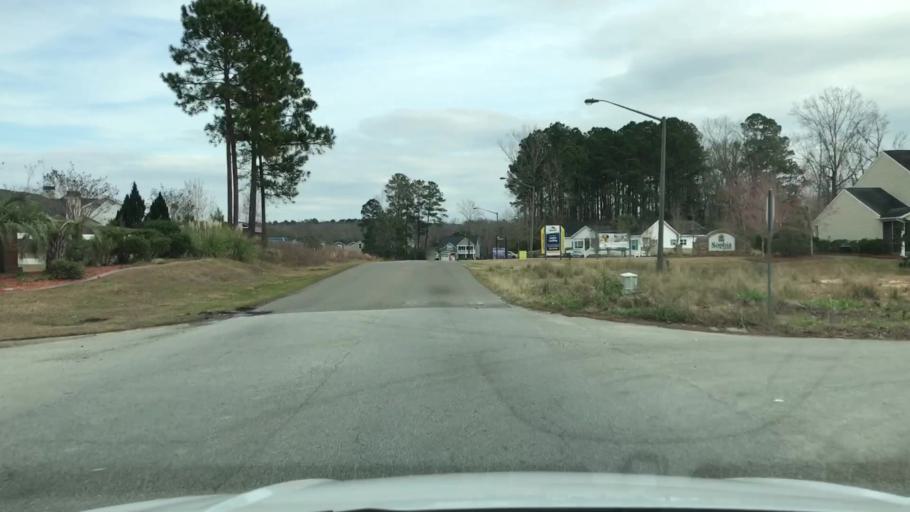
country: US
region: South Carolina
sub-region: Berkeley County
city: Goose Creek
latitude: 33.0323
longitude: -80.0234
